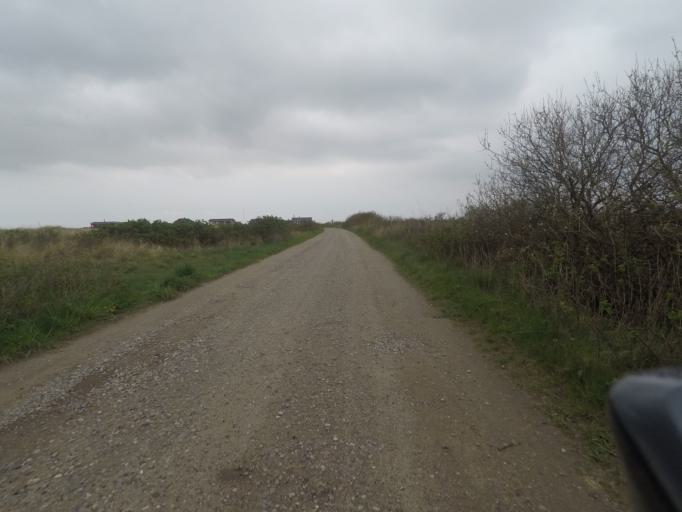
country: DE
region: Schleswig-Holstein
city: List
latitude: 55.1489
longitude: 8.4988
